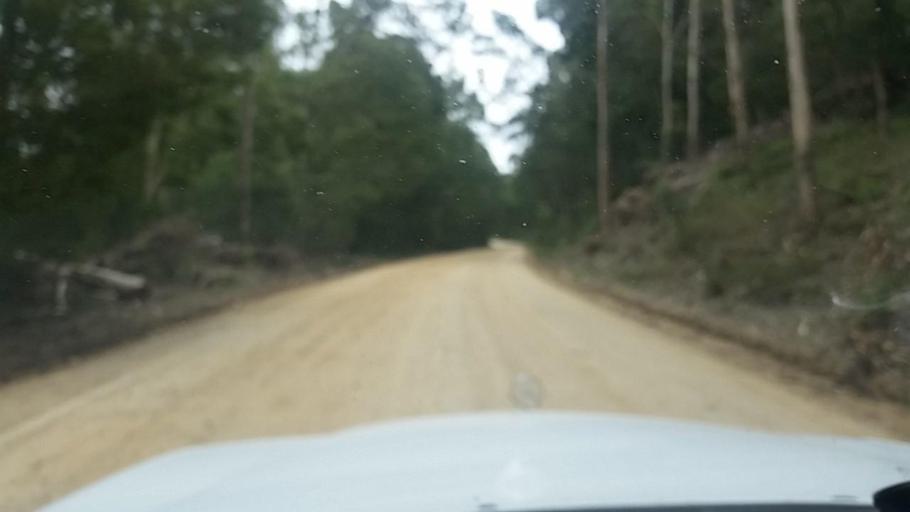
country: ZA
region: Western Cape
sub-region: Eden District Municipality
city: Knysna
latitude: -33.9898
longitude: 23.1456
